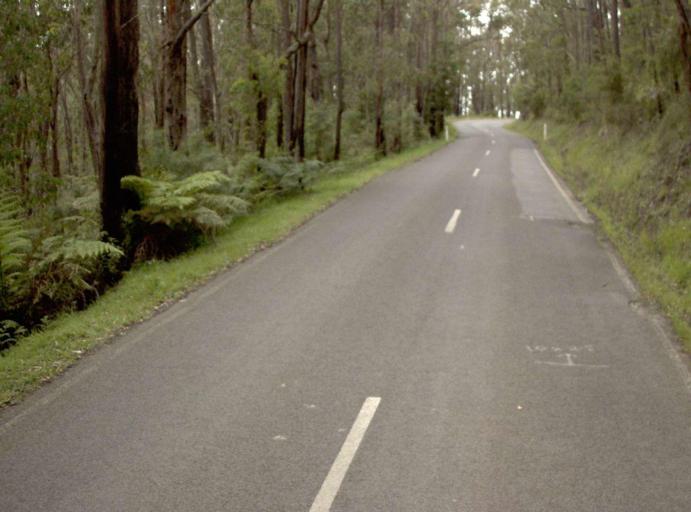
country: AU
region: Victoria
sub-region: Latrobe
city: Moe
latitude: -37.9326
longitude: 146.1142
